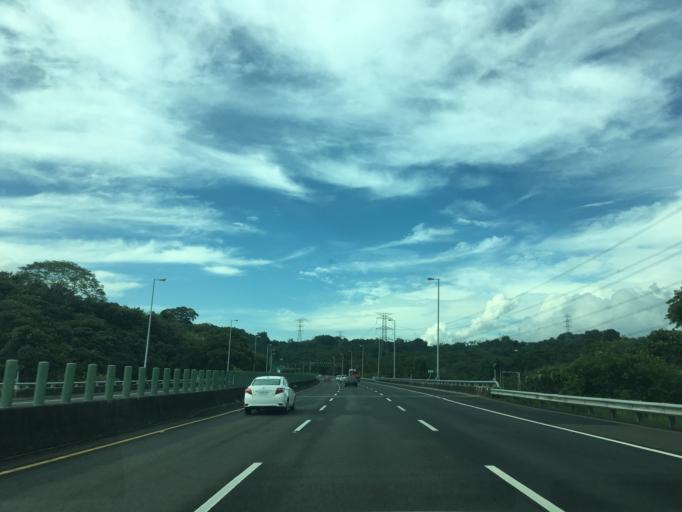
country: TW
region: Taiwan
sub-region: Chiayi
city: Jiayi Shi
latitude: 23.4678
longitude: 120.4988
